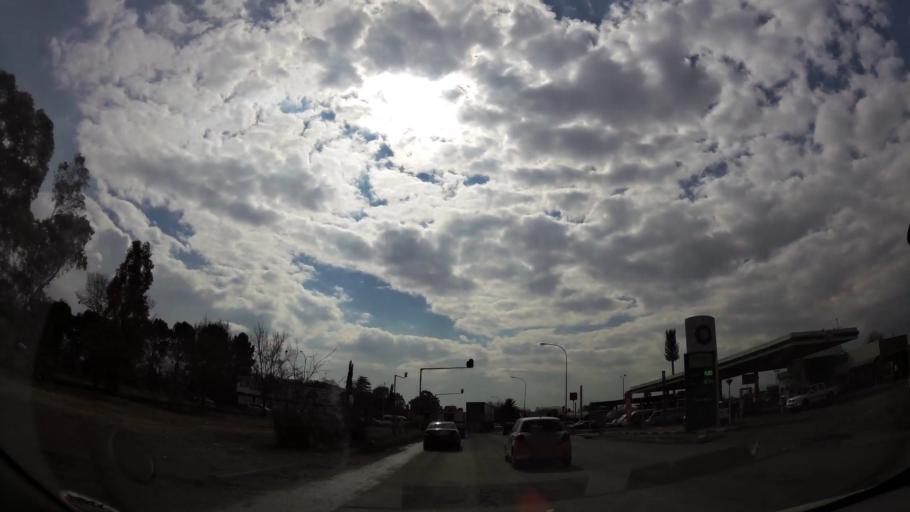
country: ZA
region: Gauteng
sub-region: Sedibeng District Municipality
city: Vereeniging
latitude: -26.6749
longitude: 27.9184
